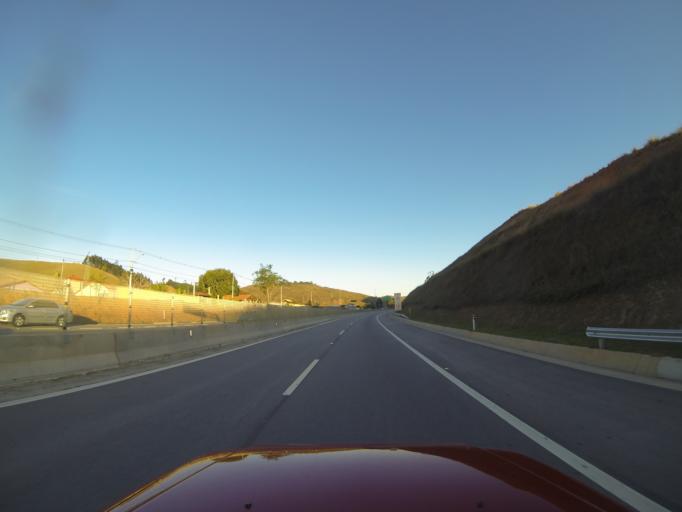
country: BR
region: Sao Paulo
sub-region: Caraguatatuba
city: Caraguatatuba
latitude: -23.4562
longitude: -45.5936
